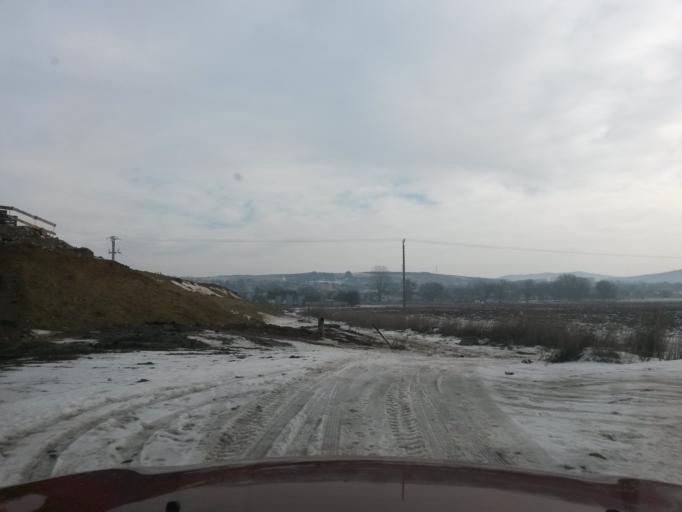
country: SK
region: Kosicky
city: Kosice
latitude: 48.7495
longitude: 21.3319
